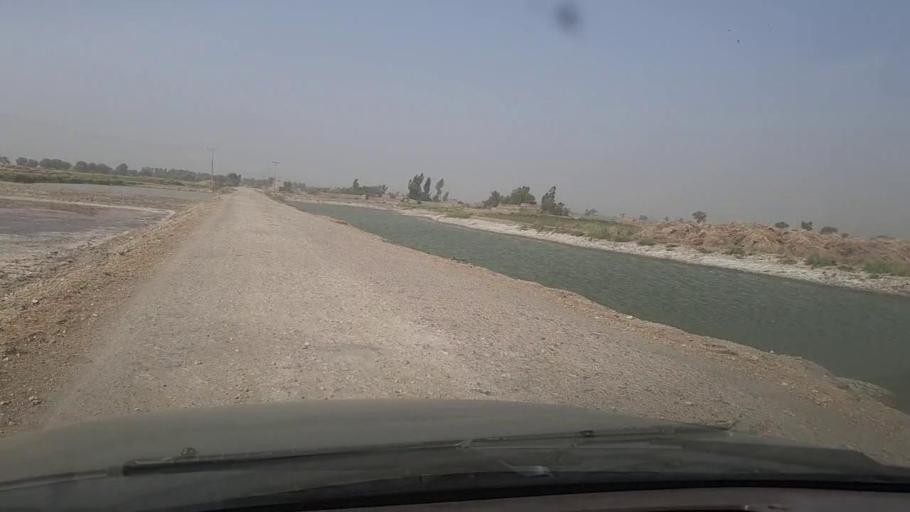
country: PK
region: Sindh
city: Garhi Yasin
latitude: 27.8796
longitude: 68.5675
